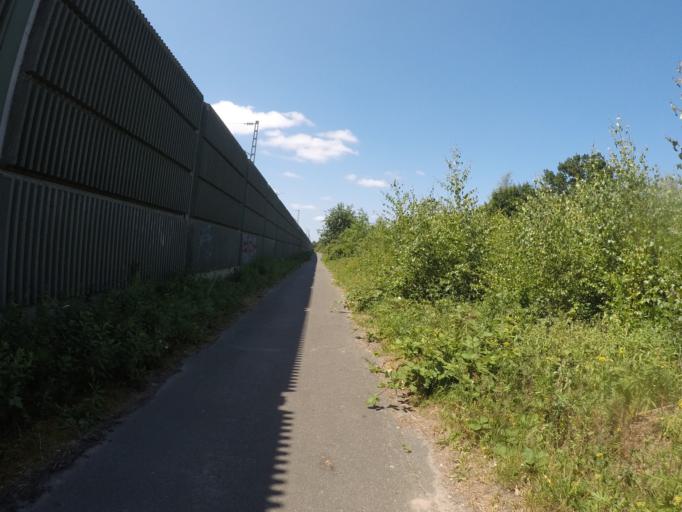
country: DE
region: Lower Saxony
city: Neu Wulmstorf
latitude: 53.4743
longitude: 9.8520
